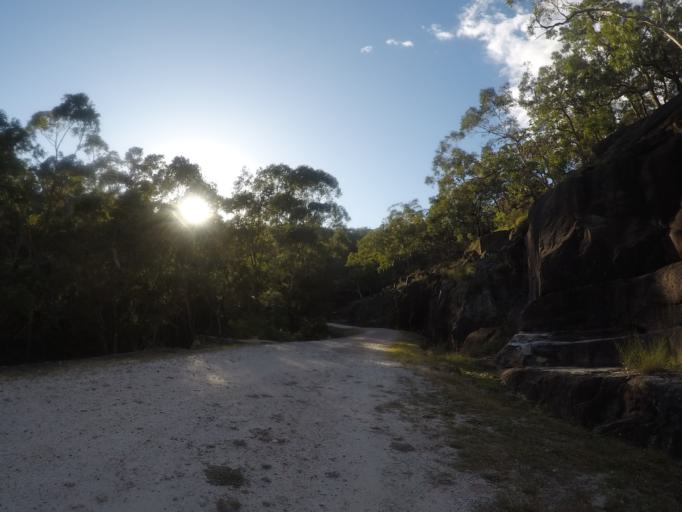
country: AU
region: New South Wales
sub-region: Hornsby Shire
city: Glenorie
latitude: -33.3687
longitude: 150.9862
